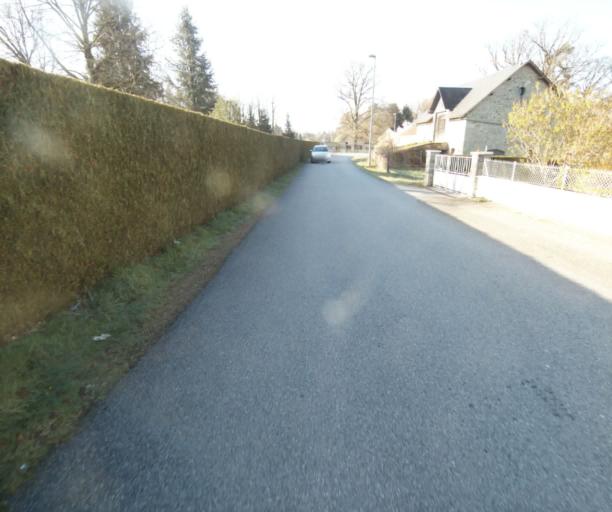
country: FR
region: Limousin
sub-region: Departement de la Correze
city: Correze
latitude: 45.3311
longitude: 1.8761
